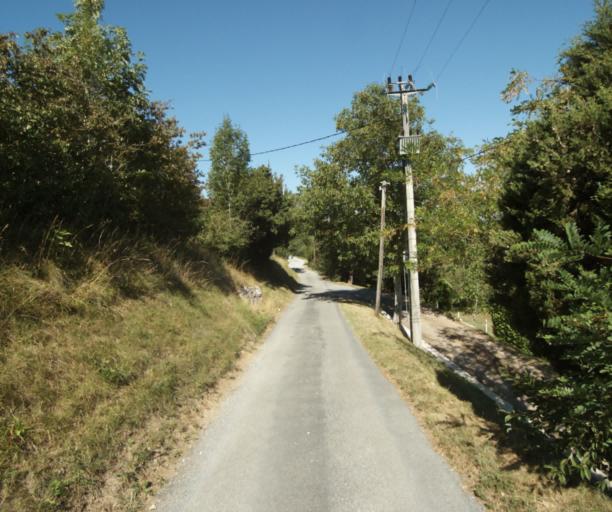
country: FR
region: Midi-Pyrenees
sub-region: Departement du Tarn
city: Soreze
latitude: 43.4468
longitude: 2.0487
